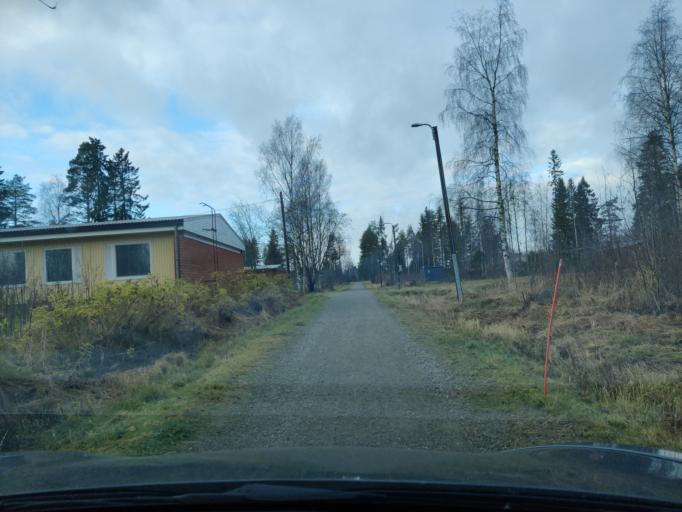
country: FI
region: Northern Savo
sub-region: Ylae-Savo
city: Kiuruvesi
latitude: 63.6444
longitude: 26.6413
